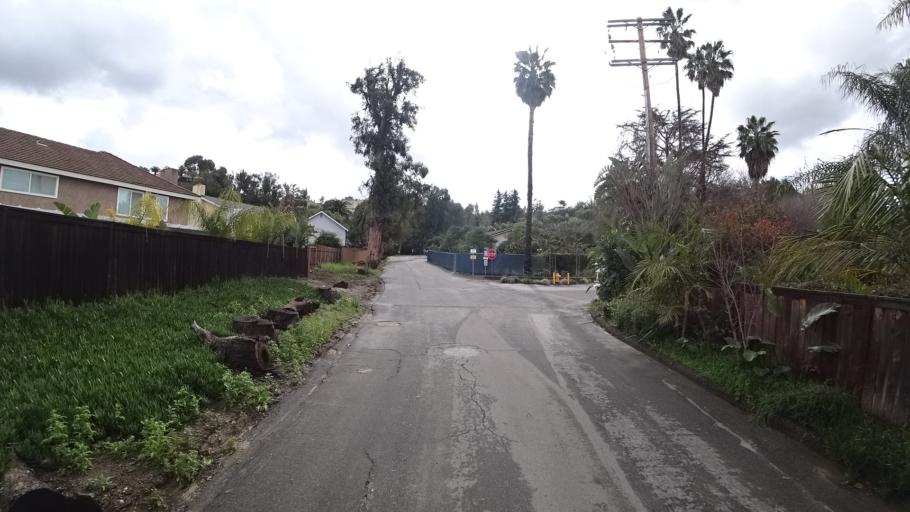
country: US
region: California
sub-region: Orange County
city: Yorba Linda
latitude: 33.8523
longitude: -117.7740
